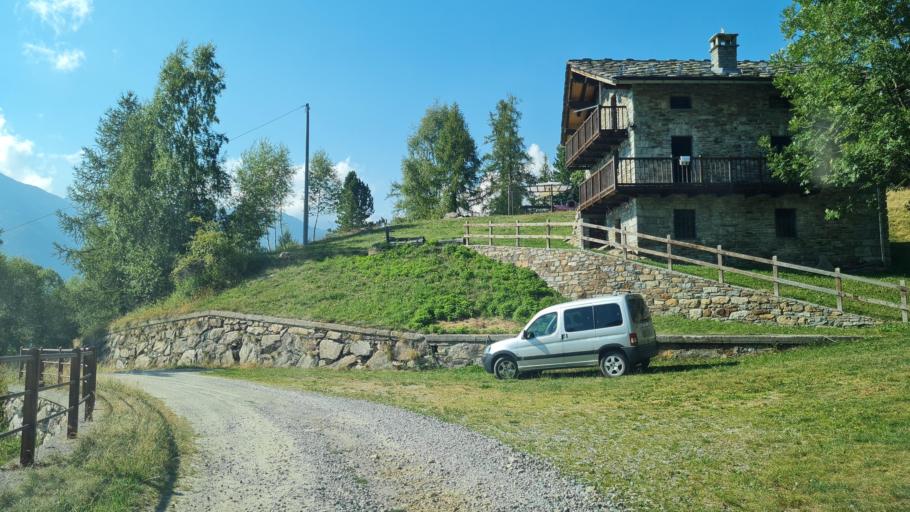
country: IT
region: Aosta Valley
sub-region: Valle d'Aosta
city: Fontainemore
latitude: 45.6294
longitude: 7.8669
